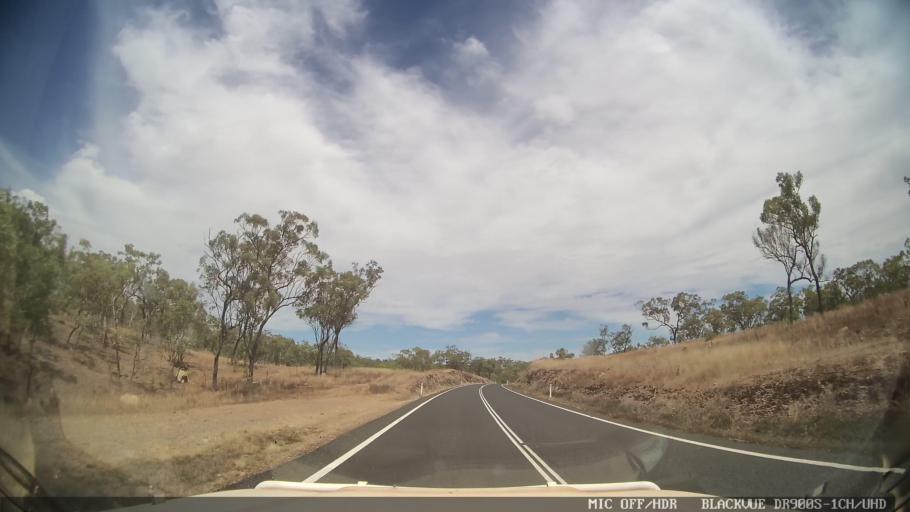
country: AU
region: Queensland
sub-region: Cairns
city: Port Douglas
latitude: -16.1484
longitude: 144.7668
